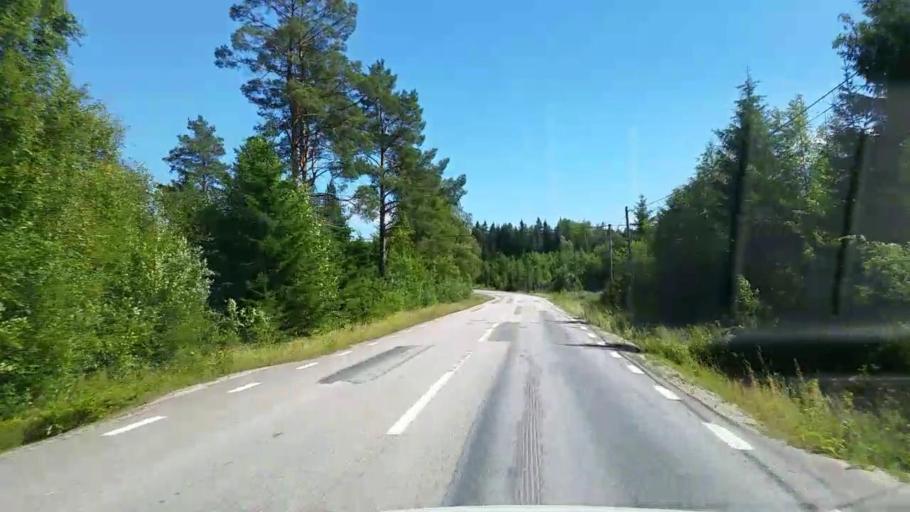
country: SE
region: Gaevleborg
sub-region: Ovanakers Kommun
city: Edsbyn
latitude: 61.3297
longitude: 15.8374
